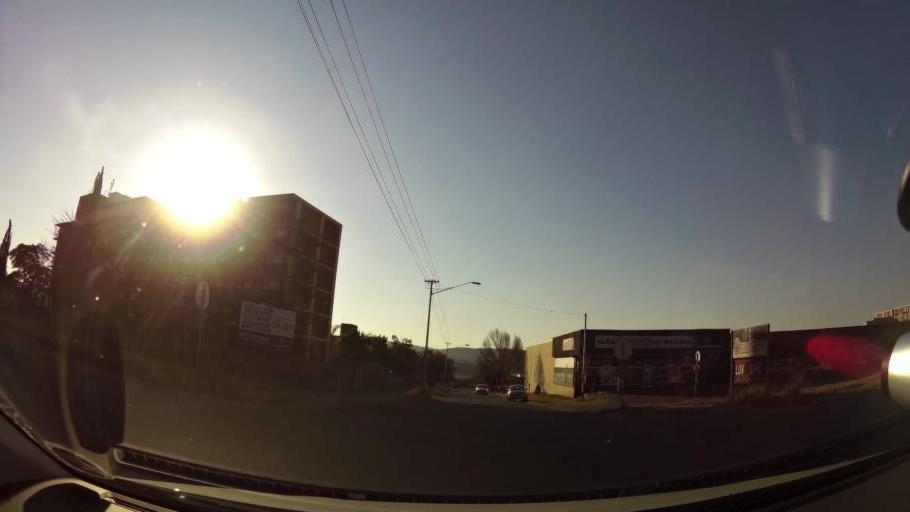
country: ZA
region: Gauteng
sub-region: City of Tshwane Metropolitan Municipality
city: Pretoria
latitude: -25.7574
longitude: 28.1147
